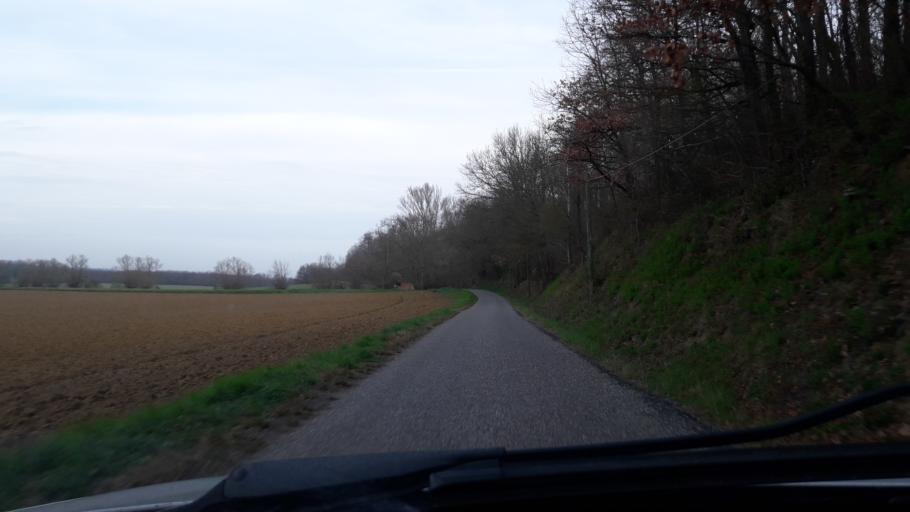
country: FR
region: Midi-Pyrenees
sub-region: Departement de la Haute-Garonne
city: Montesquieu-Volvestre
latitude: 43.1846
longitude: 1.2615
